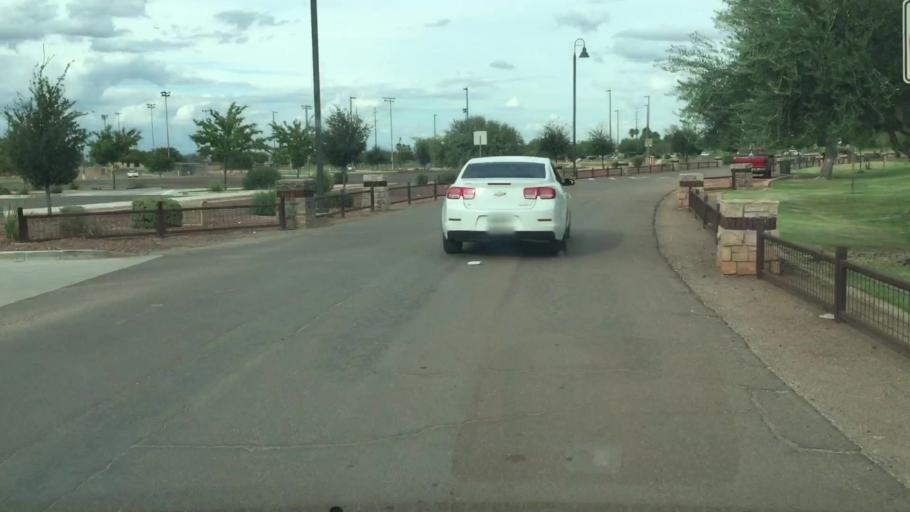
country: US
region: Arizona
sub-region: Maricopa County
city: Laveen
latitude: 33.3729
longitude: -112.1416
